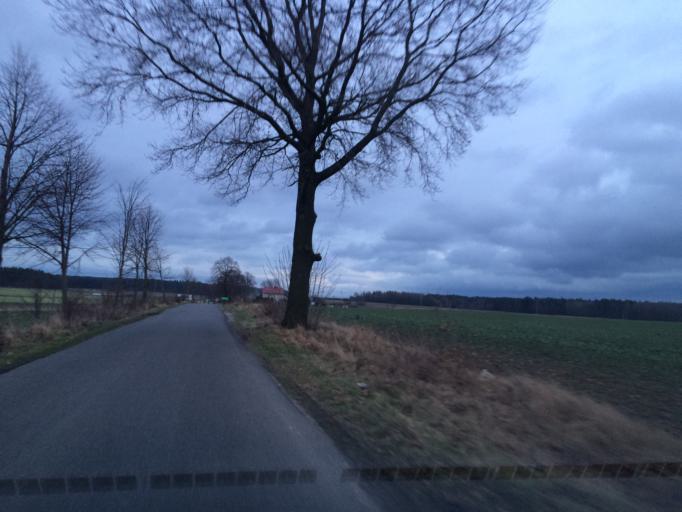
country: PL
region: Lower Silesian Voivodeship
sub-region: Powiat boleslawiecki
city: Nowogrodziec
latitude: 51.1984
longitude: 15.4318
